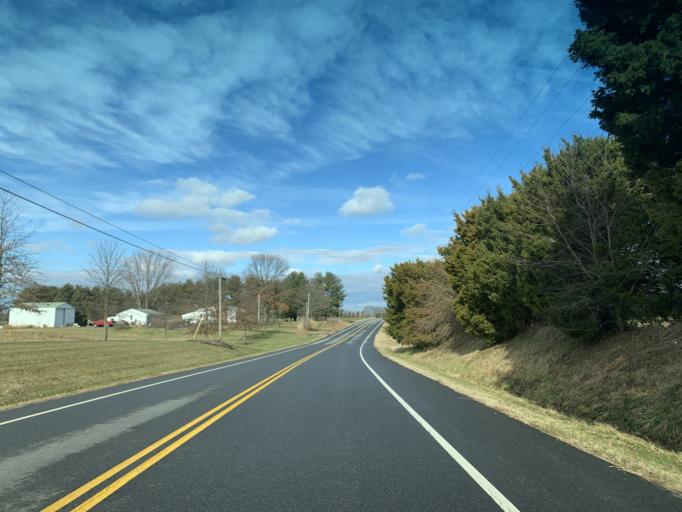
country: US
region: Maryland
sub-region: Kent County
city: Chestertown
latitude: 39.3399
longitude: -76.0620
